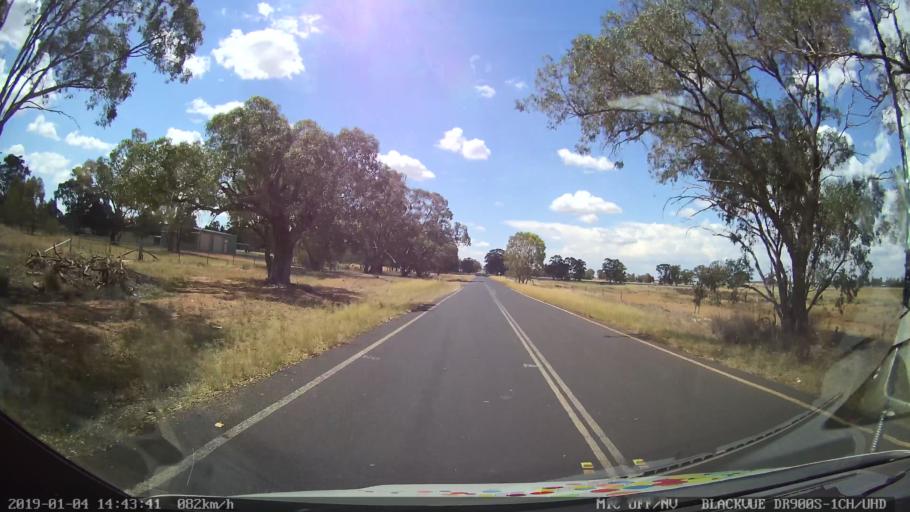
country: AU
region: New South Wales
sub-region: Dubbo Municipality
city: Dubbo
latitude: -32.1160
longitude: 148.6539
